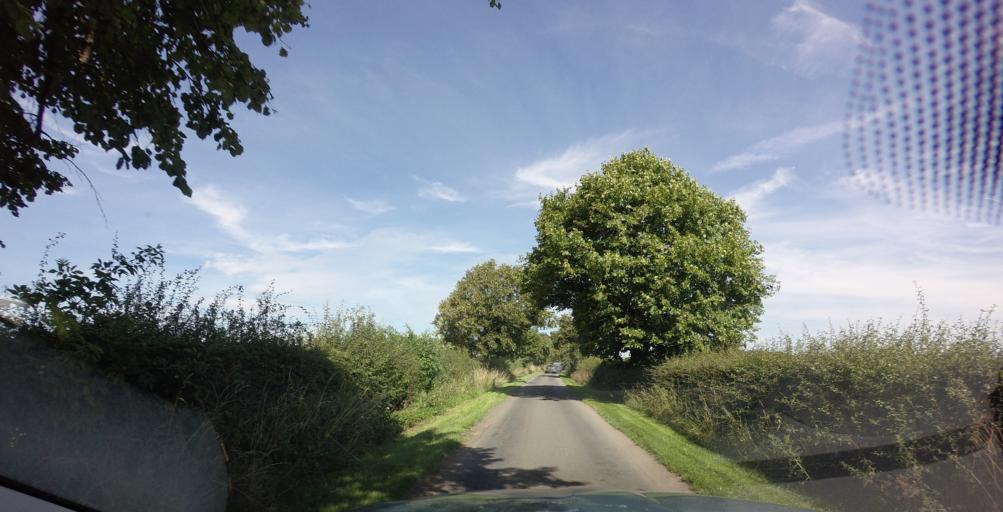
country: GB
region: England
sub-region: North Yorkshire
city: Ripon
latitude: 54.1184
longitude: -1.4835
